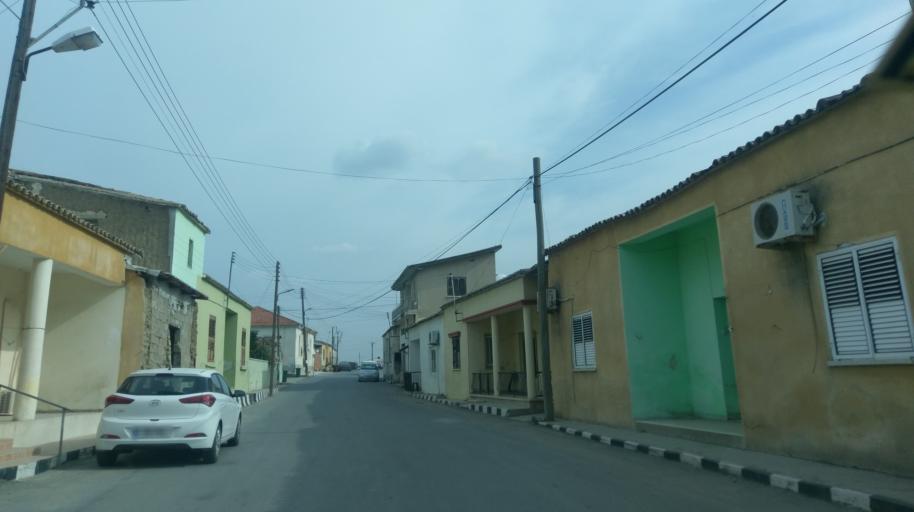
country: CY
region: Ammochostos
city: Lefkonoiko
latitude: 35.2600
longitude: 33.7356
